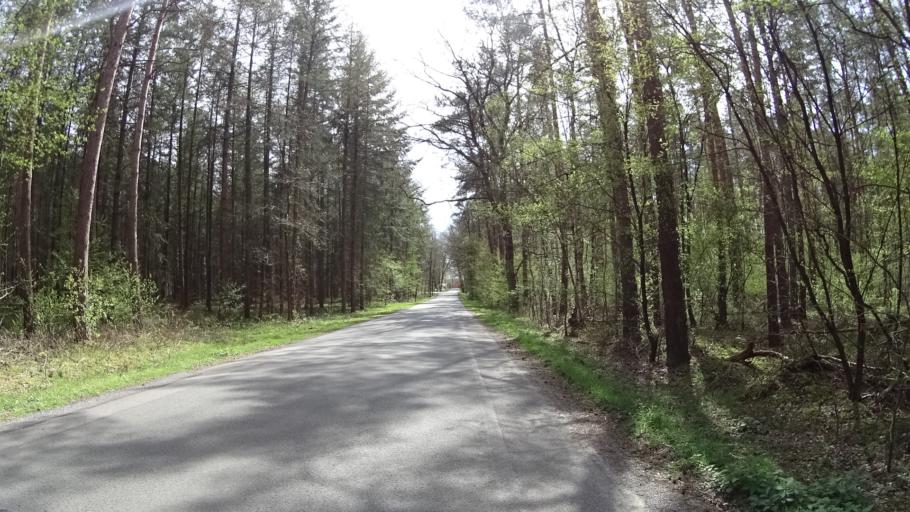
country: DE
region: Lower Saxony
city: Emsburen
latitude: 52.4346
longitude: 7.3502
